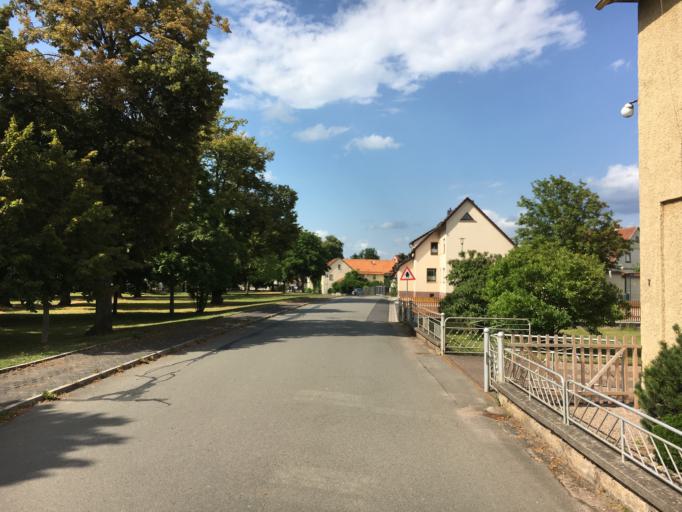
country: DE
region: Thuringia
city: Barchfeld
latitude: 50.7989
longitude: 10.3043
